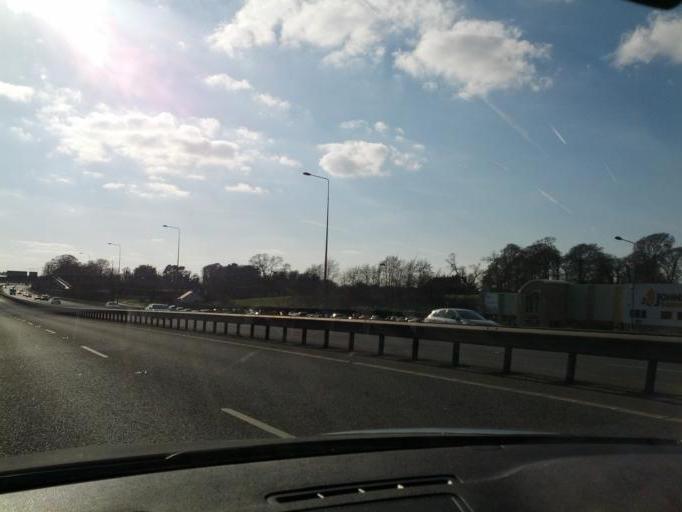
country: IE
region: Leinster
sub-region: Kildare
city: Johnstown
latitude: 53.2380
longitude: -6.6214
